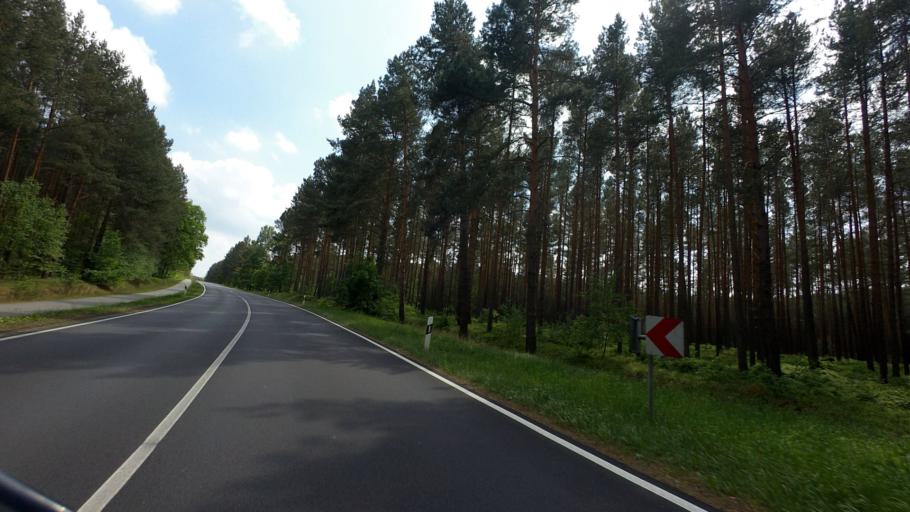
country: DE
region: Saxony
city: Niesky
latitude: 51.3255
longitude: 14.8200
